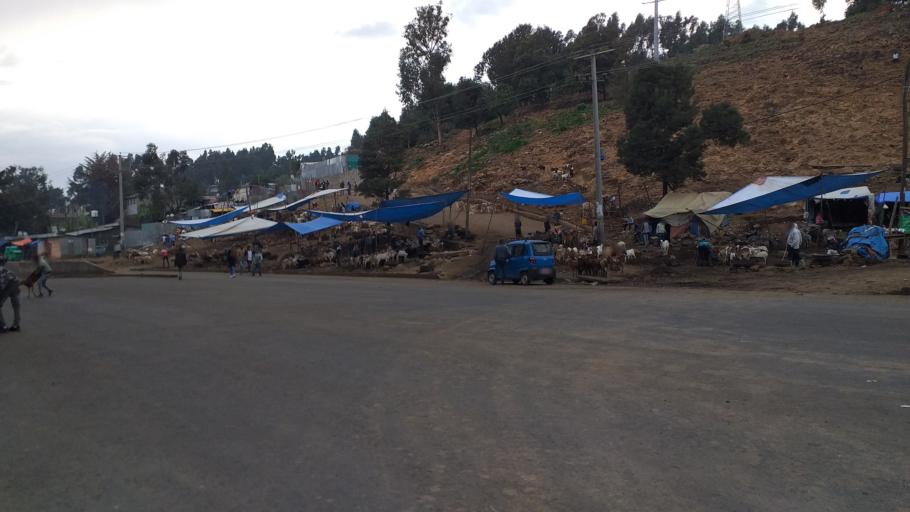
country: ET
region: Adis Abeba
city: Addis Ababa
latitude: 9.0305
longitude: 38.8210
